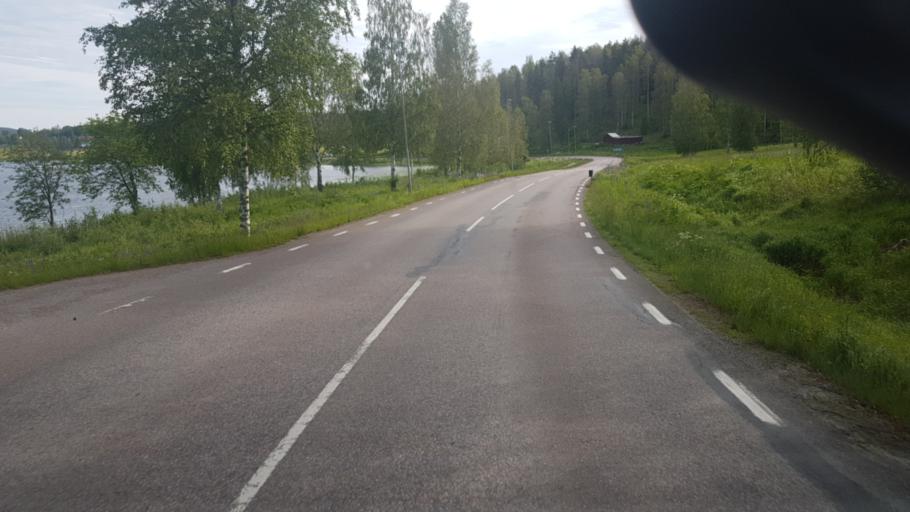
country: SE
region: Vaermland
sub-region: Arvika Kommun
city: Arvika
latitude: 59.7806
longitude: 12.6176
